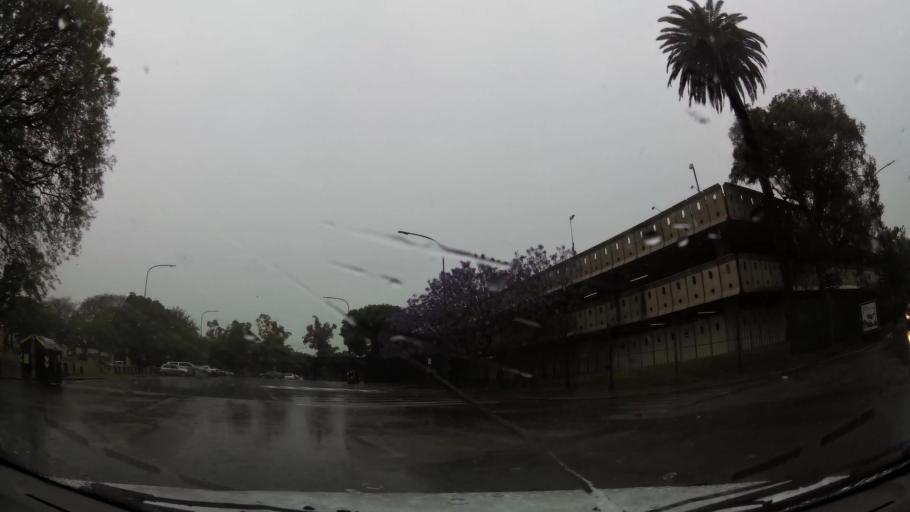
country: AR
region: Buenos Aires F.D.
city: Colegiales
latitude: -34.5687
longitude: -58.4218
